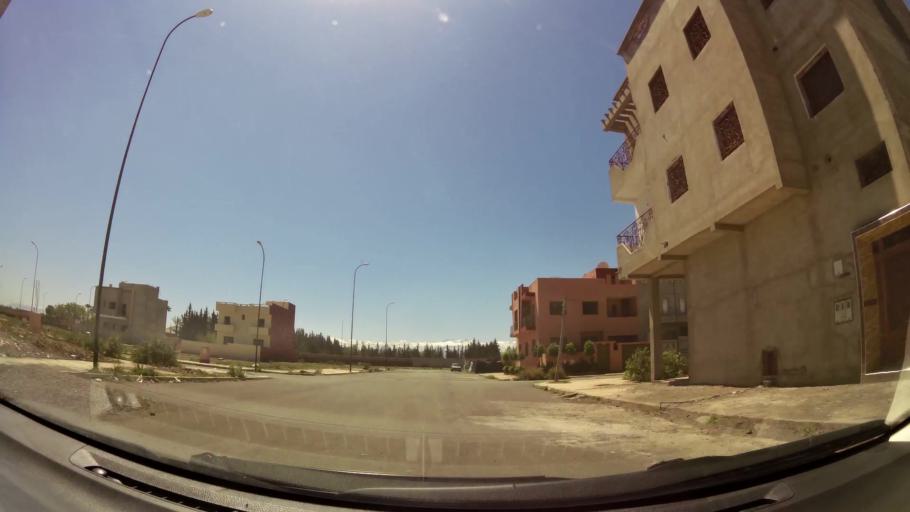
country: MA
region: Marrakech-Tensift-Al Haouz
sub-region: Marrakech
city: Marrakesh
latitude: 31.5507
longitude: -7.9777
